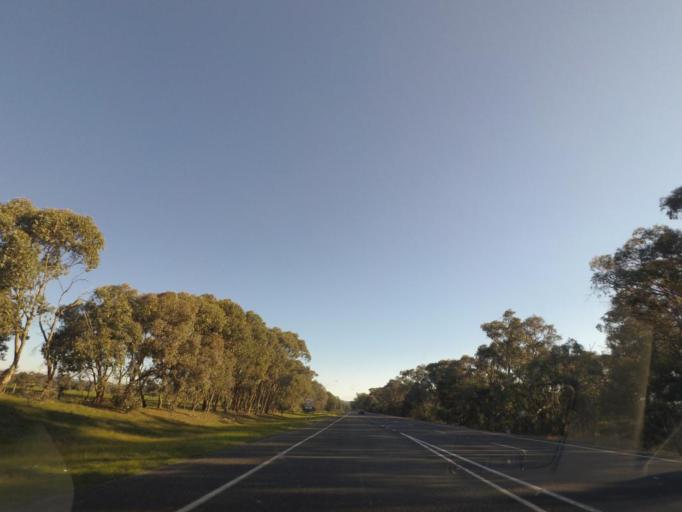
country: AU
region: Victoria
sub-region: Greater Shepparton
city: Shepparton
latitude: -36.7832
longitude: 145.4983
